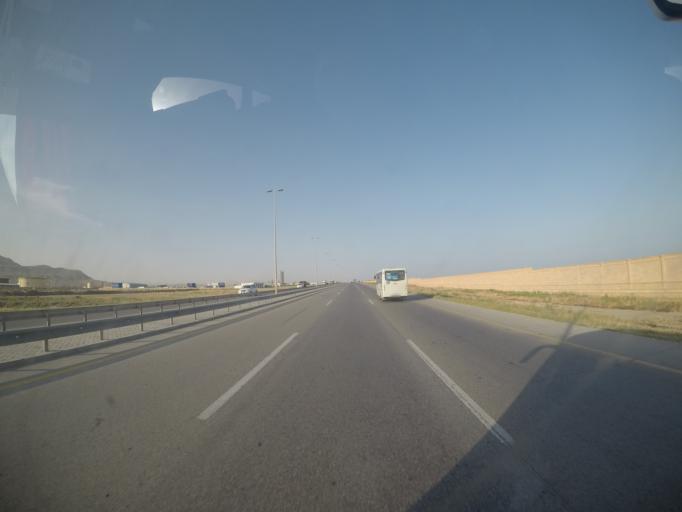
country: AZ
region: Baki
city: Korgoz
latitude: 40.2077
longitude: 49.5354
